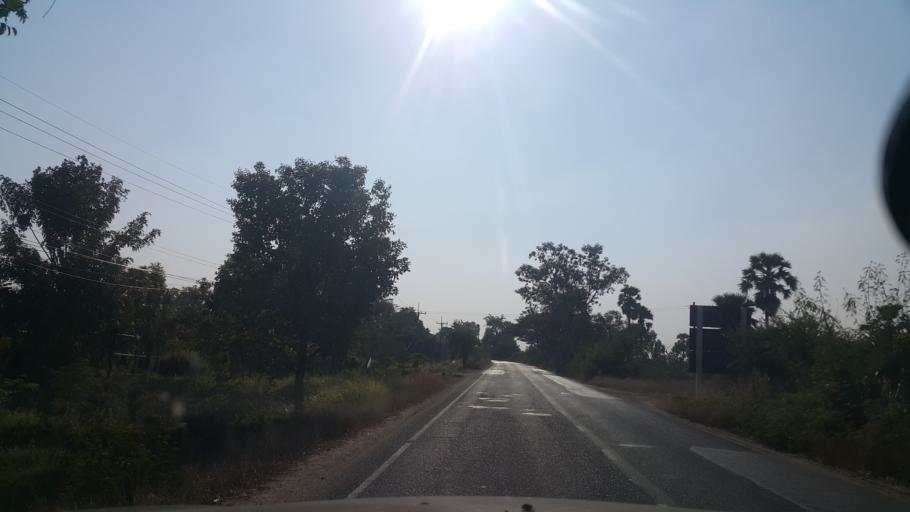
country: TH
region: Nakhon Ratchasima
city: Phimai
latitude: 15.2074
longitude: 102.4433
